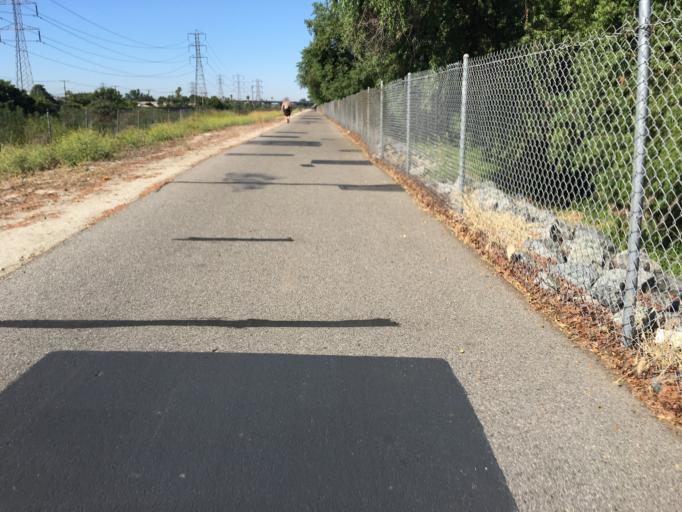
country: US
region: California
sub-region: Los Angeles County
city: West Whittier-Los Nietos
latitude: 33.9739
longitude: -118.0837
